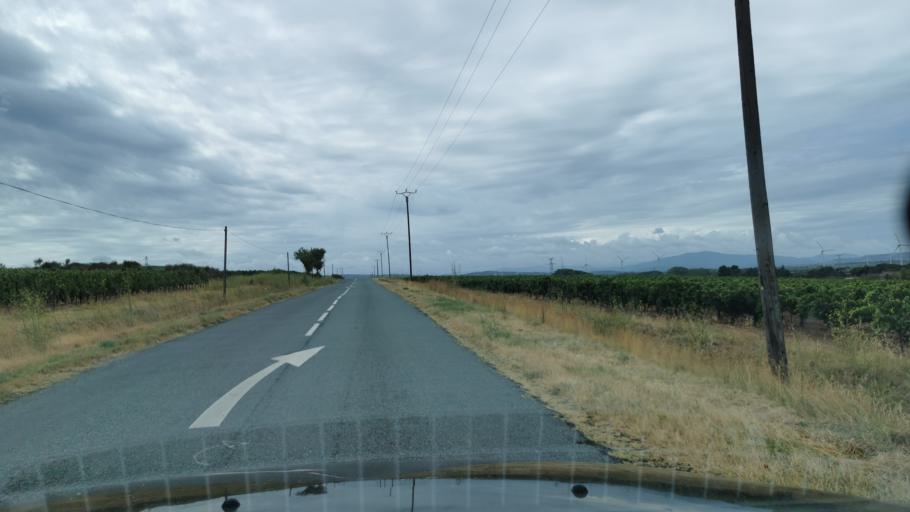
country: FR
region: Languedoc-Roussillon
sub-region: Departement de l'Aude
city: Nevian
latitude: 43.2056
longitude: 2.8728
